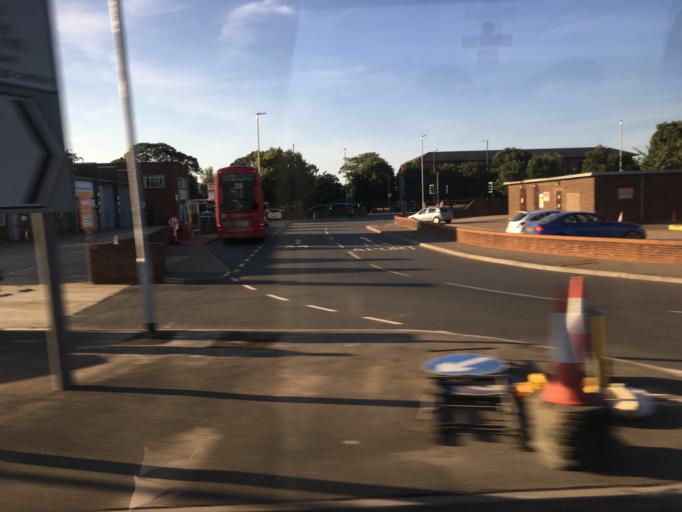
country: GB
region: England
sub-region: Greater London
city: West Drayton
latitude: 51.4800
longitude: -0.4592
